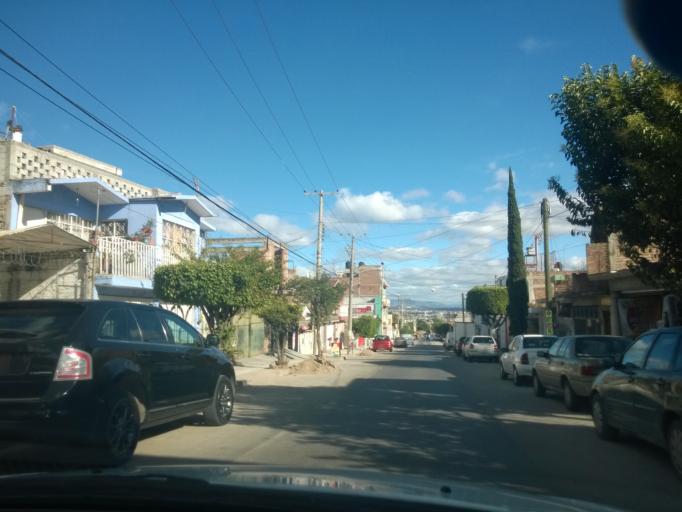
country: MX
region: Guanajuato
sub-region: Leon
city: Ejido la Joya
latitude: 21.1169
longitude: -101.7115
